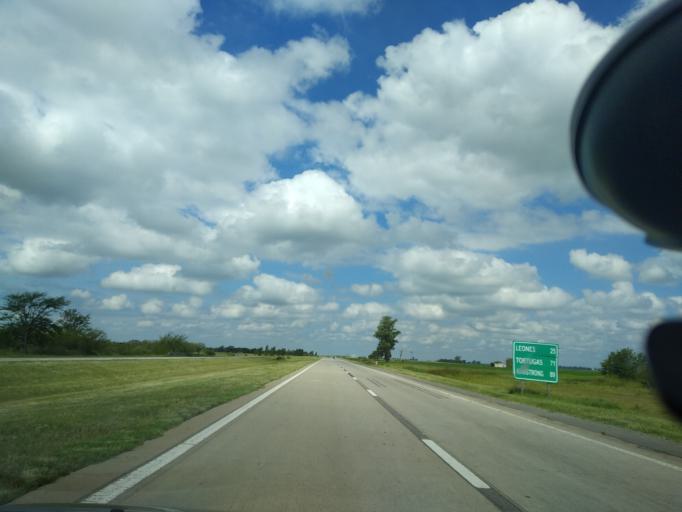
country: AR
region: Cordoba
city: Bell Ville
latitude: -32.5924
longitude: -62.5015
